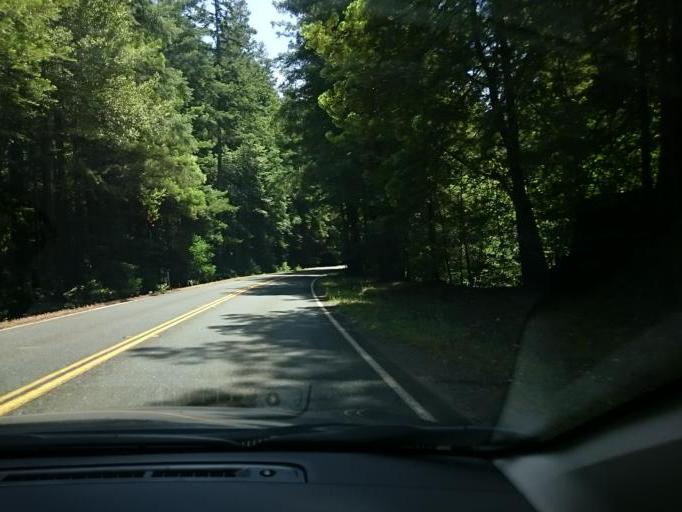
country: US
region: California
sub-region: Mendocino County
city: Boonville
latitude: 39.1607
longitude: -123.5797
